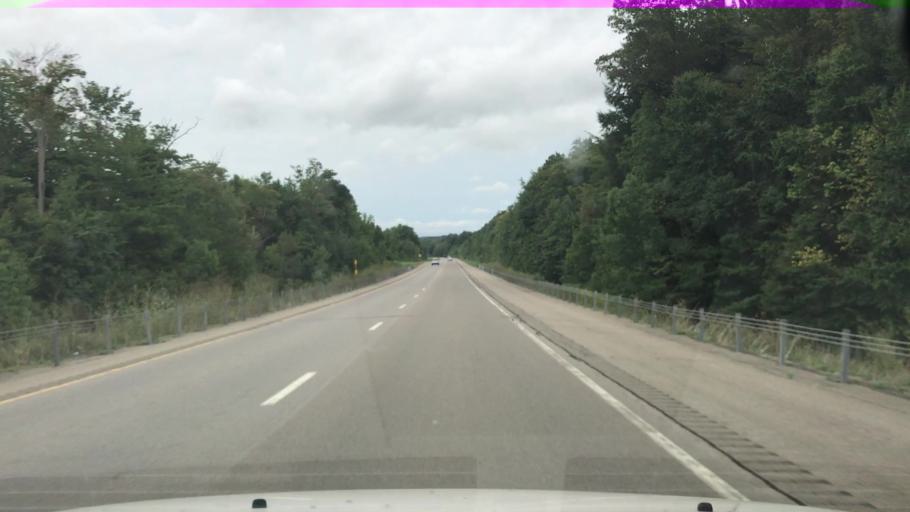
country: US
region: New York
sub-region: Erie County
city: North Boston
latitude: 42.5997
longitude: -78.7484
